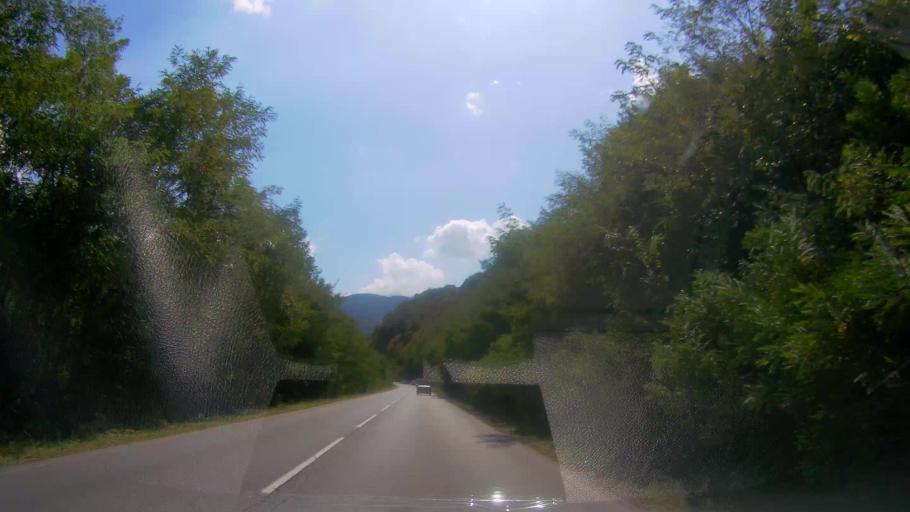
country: BG
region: Stara Zagora
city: Gurkovo
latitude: 42.7271
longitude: 25.7124
